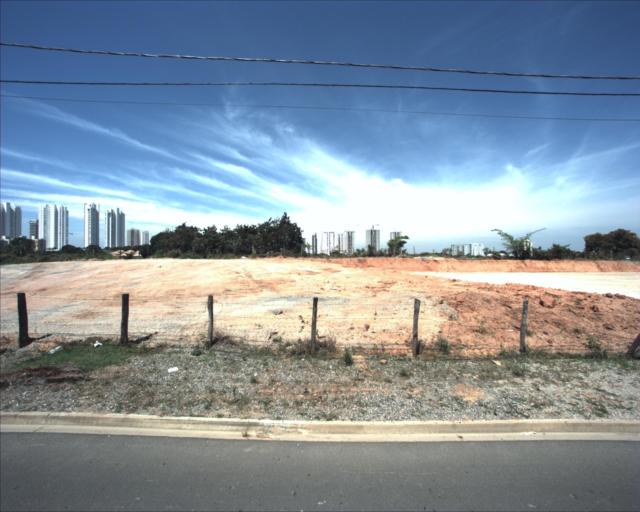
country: BR
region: Sao Paulo
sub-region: Sorocaba
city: Sorocaba
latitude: -23.5341
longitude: -47.4732
